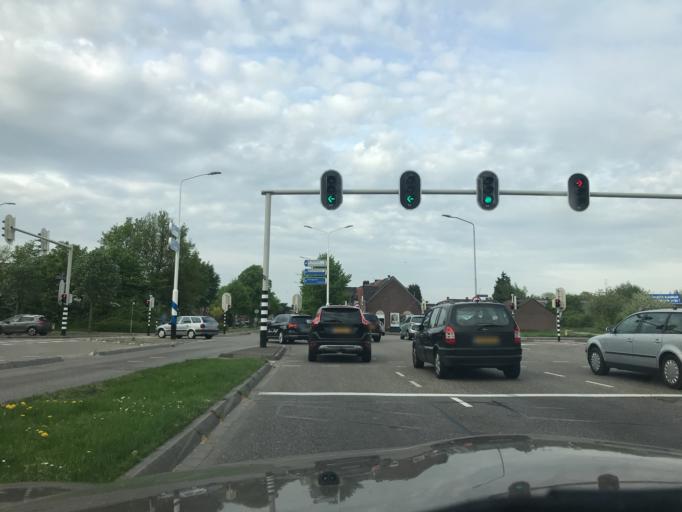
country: NL
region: Limburg
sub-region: Gemeente Venlo
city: Venlo
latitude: 51.3580
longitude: 6.1577
